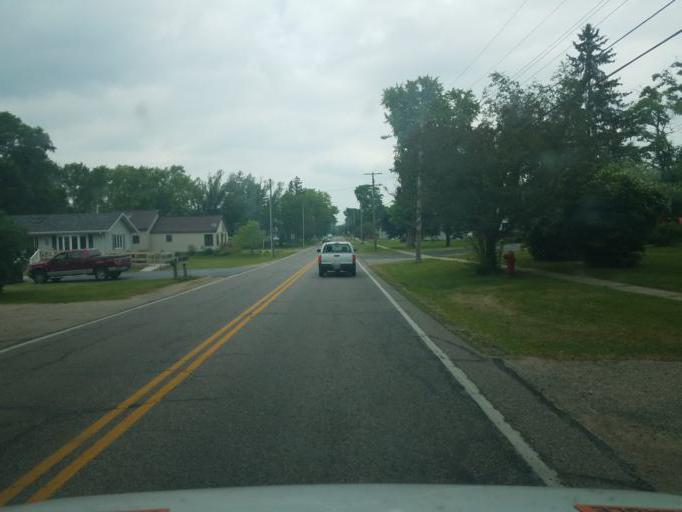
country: US
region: Wisconsin
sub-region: Juneau County
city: Elroy
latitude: 43.6437
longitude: -90.2182
